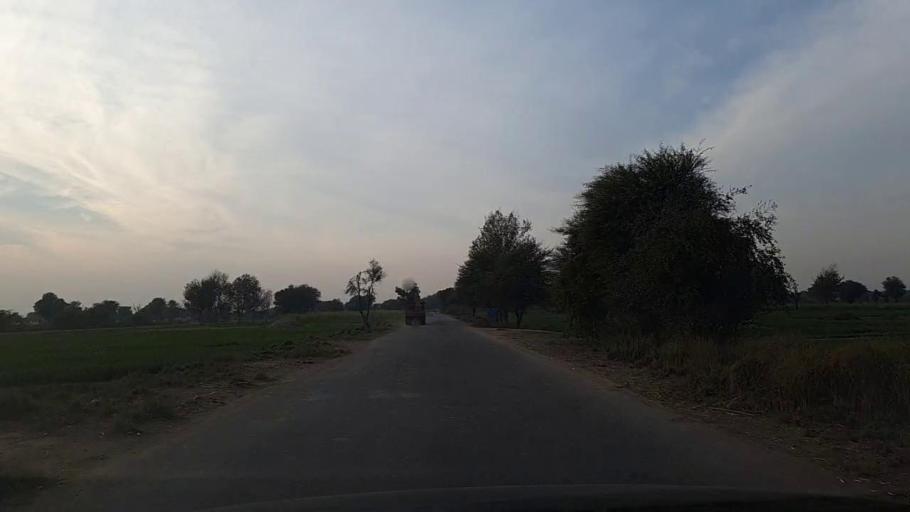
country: PK
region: Sindh
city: Nawabshah
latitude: 26.3997
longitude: 68.4744
